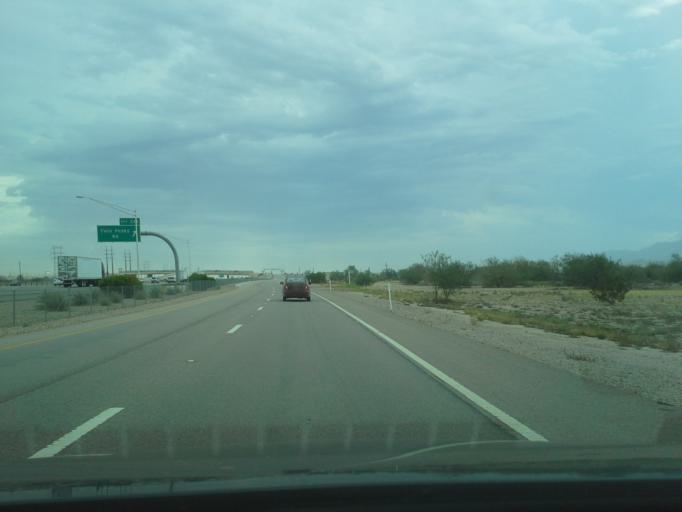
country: US
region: Arizona
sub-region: Pima County
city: Tortolita
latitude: 32.3862
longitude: -111.1160
